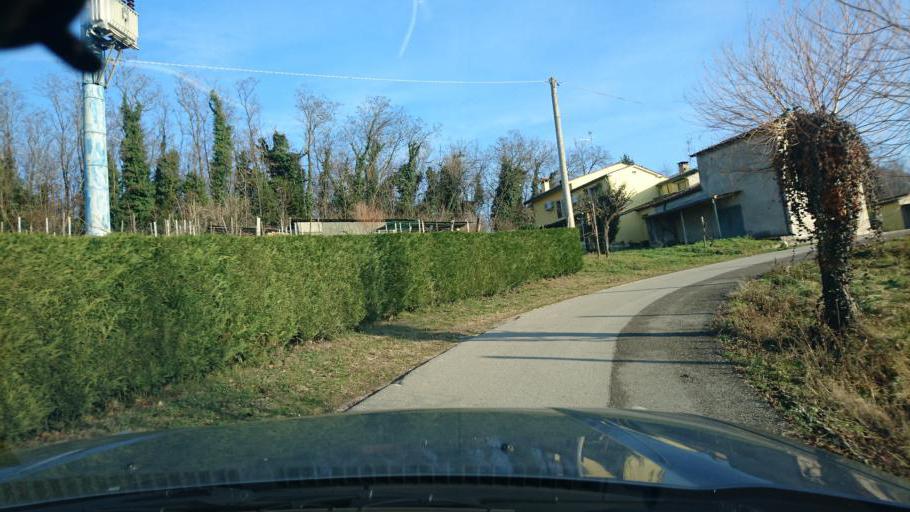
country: IT
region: Veneto
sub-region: Provincia di Padova
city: Vo
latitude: 45.3232
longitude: 11.6619
